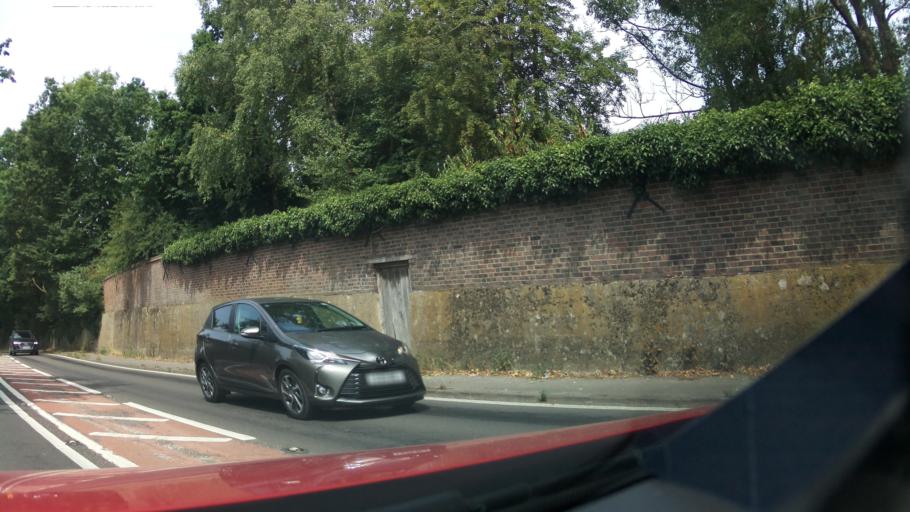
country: GB
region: England
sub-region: Surrey
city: Headley
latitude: 51.2438
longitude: -0.2527
